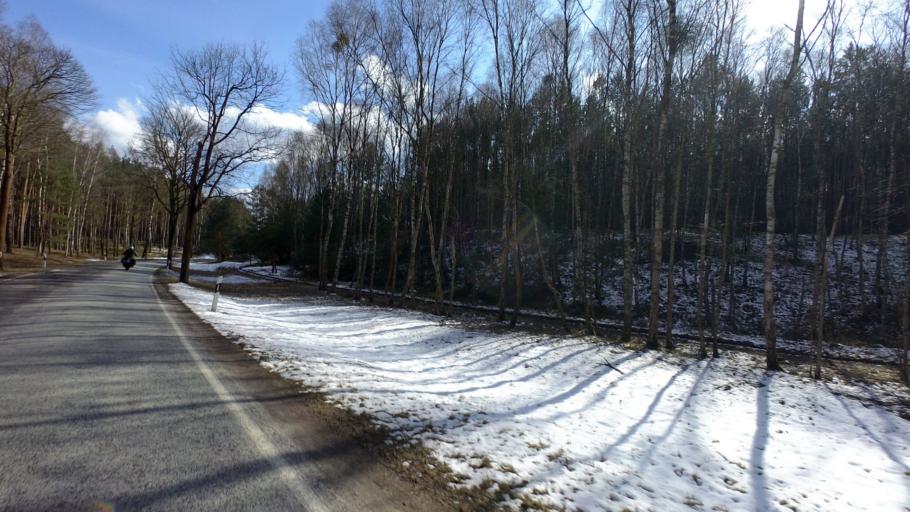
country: DE
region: Brandenburg
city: Biesenthal
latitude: 52.7917
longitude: 13.6036
